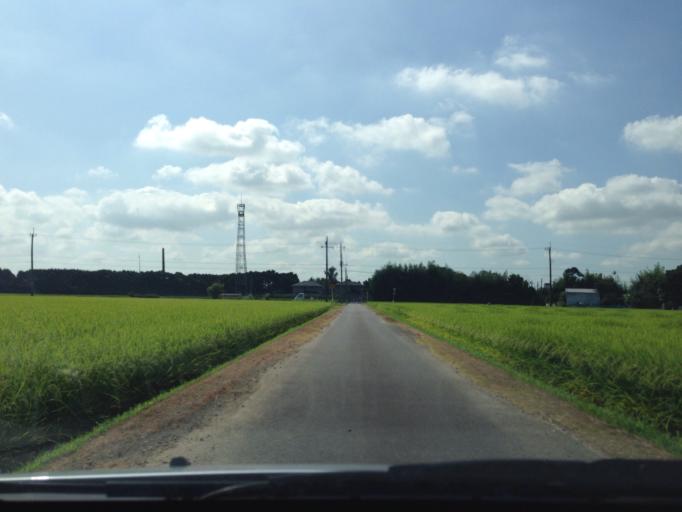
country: JP
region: Ibaraki
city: Inashiki
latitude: 36.0078
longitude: 140.3689
